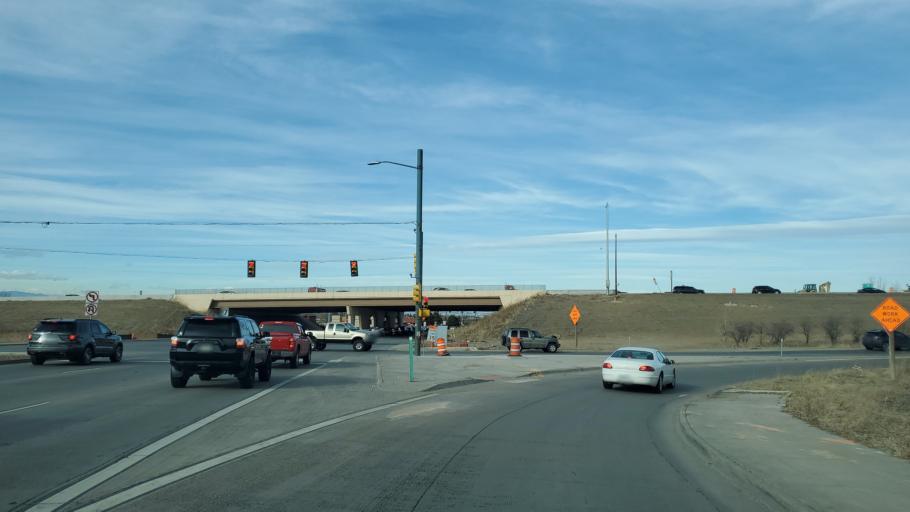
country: US
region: Colorado
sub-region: Douglas County
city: Highlands Ranch
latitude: 39.5620
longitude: -104.9601
